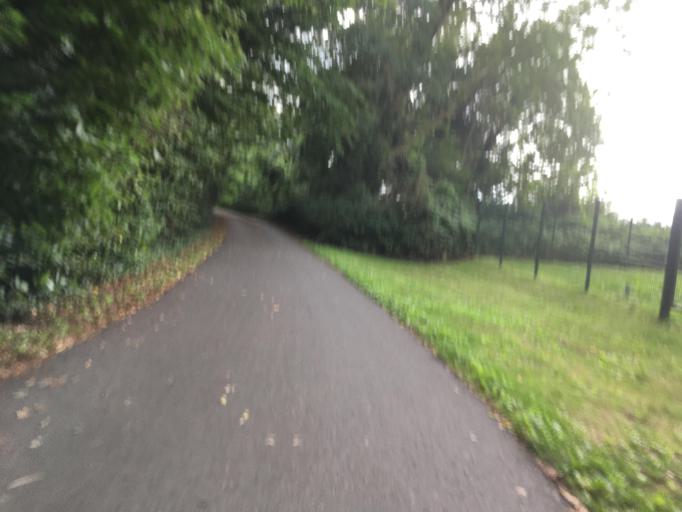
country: DE
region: Brandenburg
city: Prenzlau
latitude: 53.2972
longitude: 13.8665
